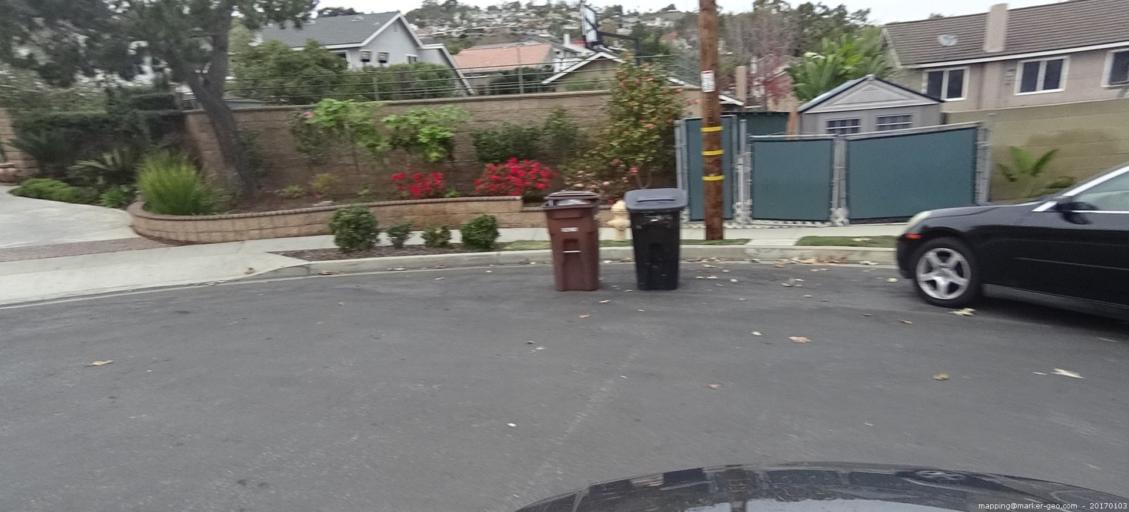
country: US
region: California
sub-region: Orange County
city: Dana Point
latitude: 33.4853
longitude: -117.6871
